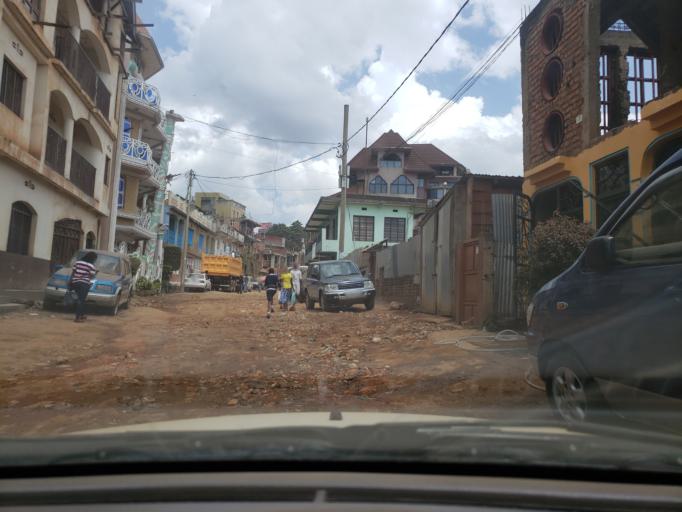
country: CD
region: South Kivu
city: Bukavu
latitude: -2.5047
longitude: 28.8630
